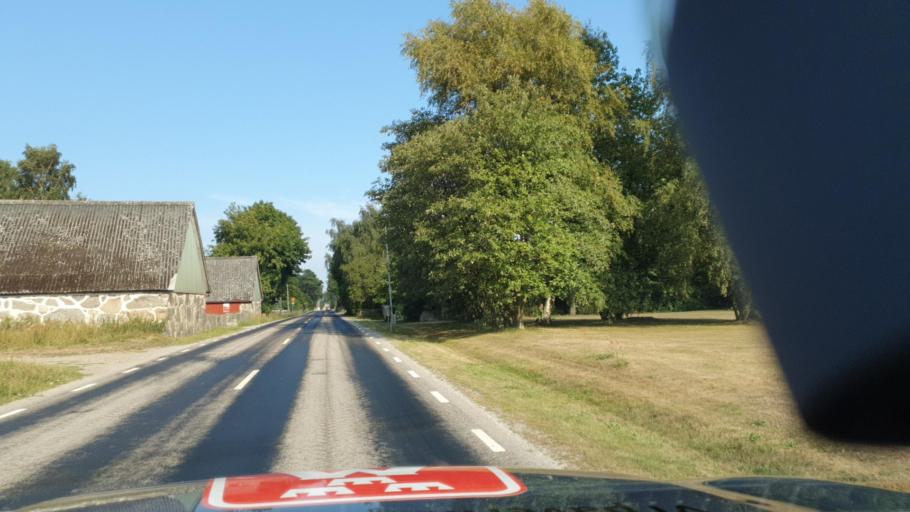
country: SE
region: Blekinge
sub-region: Solvesborgs Kommun
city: Soelvesborg
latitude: 56.0394
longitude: 14.7075
